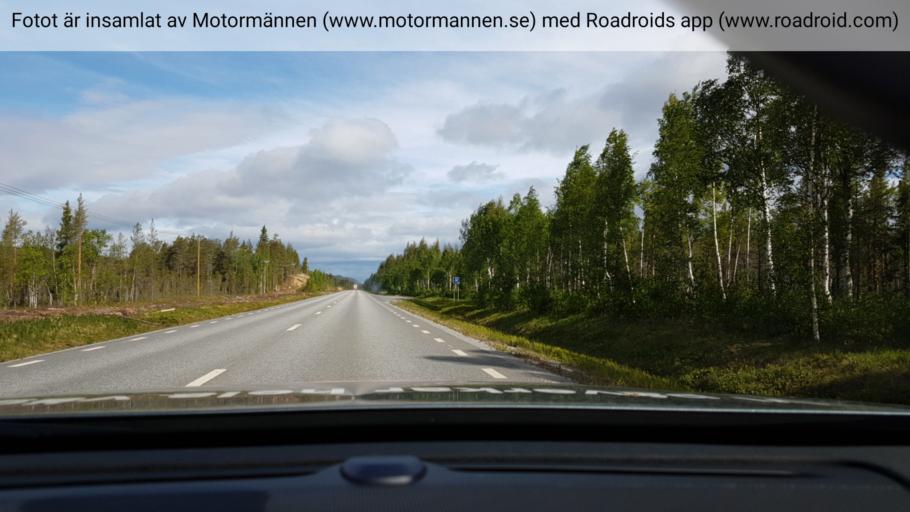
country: SE
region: Vaesterbotten
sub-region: Asele Kommun
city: Insjon
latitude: 64.1706
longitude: 17.8014
